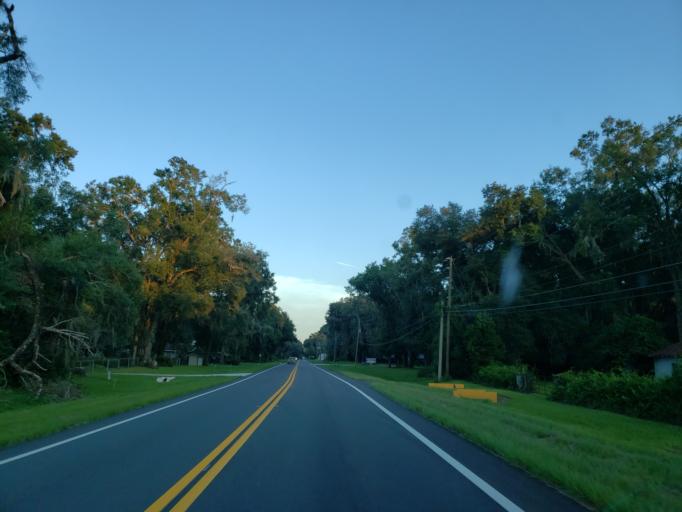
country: US
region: Florida
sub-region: Marion County
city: Citra
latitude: 29.3801
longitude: -82.2041
